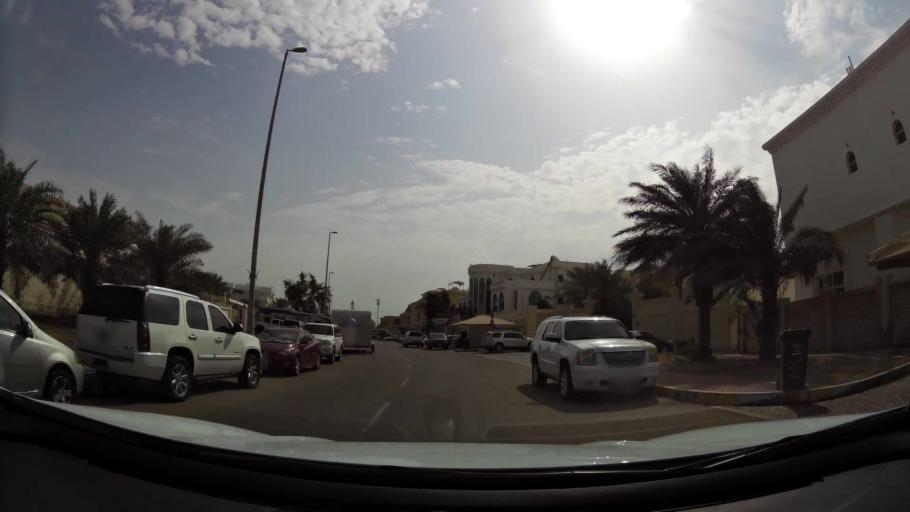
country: AE
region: Abu Dhabi
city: Abu Dhabi
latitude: 24.4425
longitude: 54.4214
